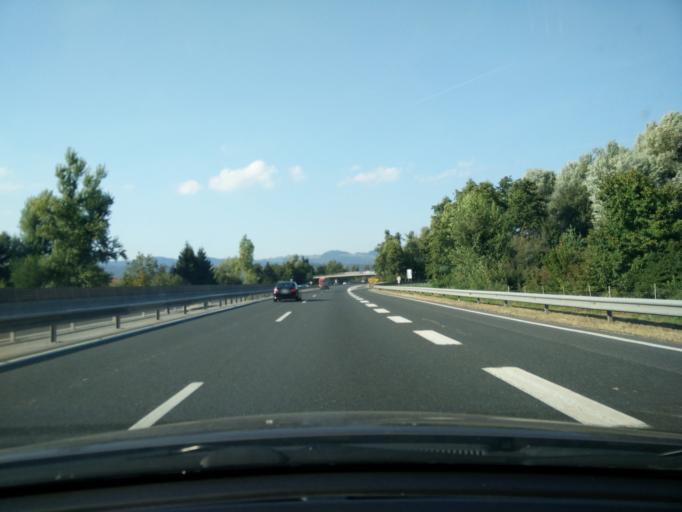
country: SI
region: Vrhnika
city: Verd
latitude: 45.9651
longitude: 14.3048
